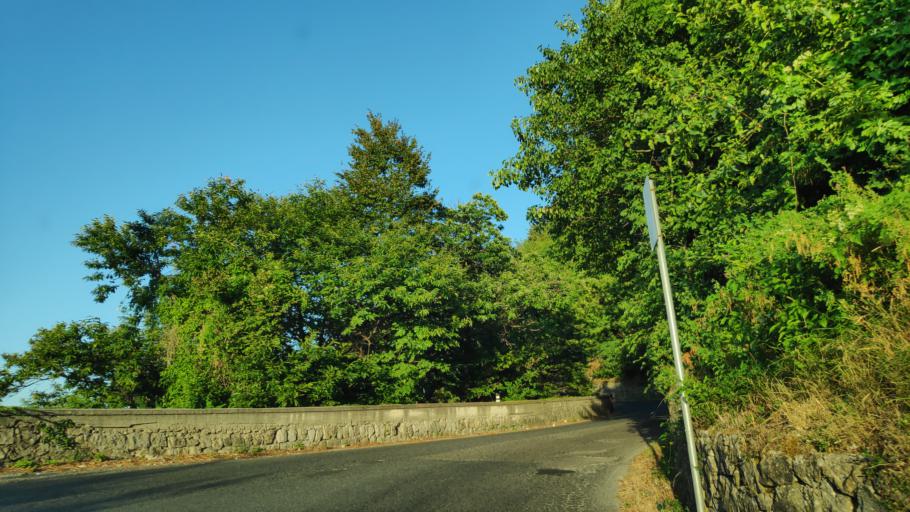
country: IT
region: Campania
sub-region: Provincia di Salerno
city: Corbara
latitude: 40.7250
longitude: 14.6044
